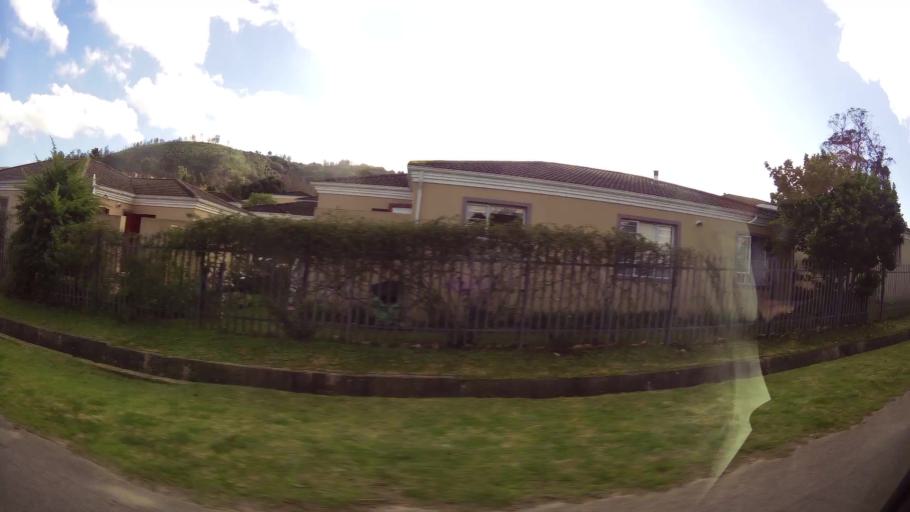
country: ZA
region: Western Cape
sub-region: Eden District Municipality
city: Knysna
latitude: -34.0398
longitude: 23.0716
